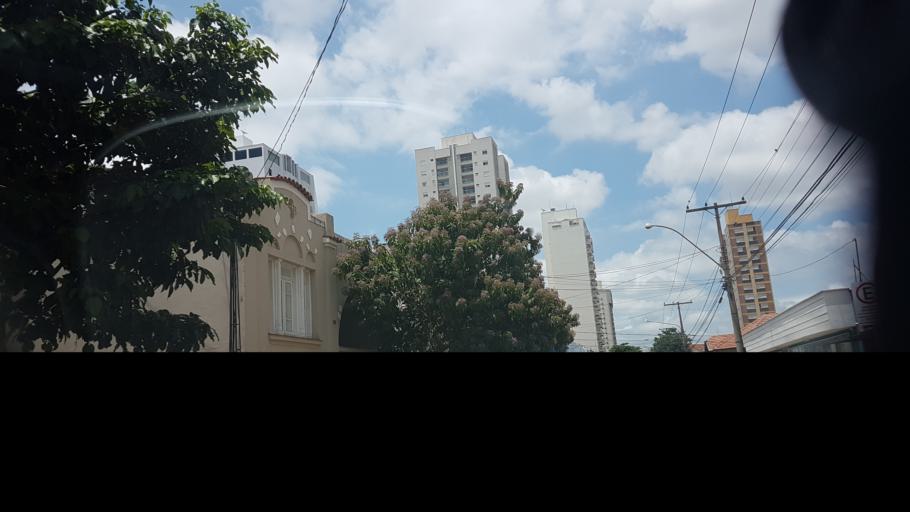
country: BR
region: Sao Paulo
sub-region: Piracicaba
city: Piracicaba
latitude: -22.7195
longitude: -47.6511
